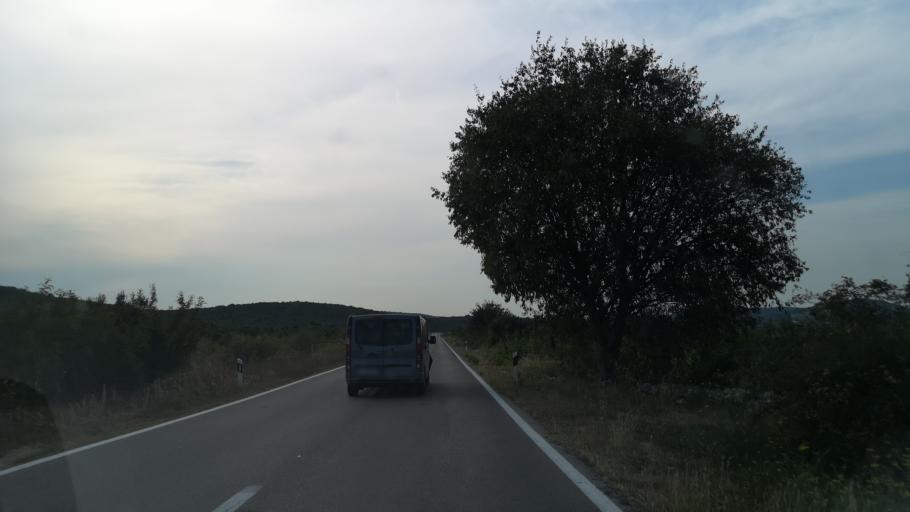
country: HR
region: Sibensko-Kniniska
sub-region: Grad Sibenik
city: Pirovac
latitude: 43.8587
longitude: 15.7526
